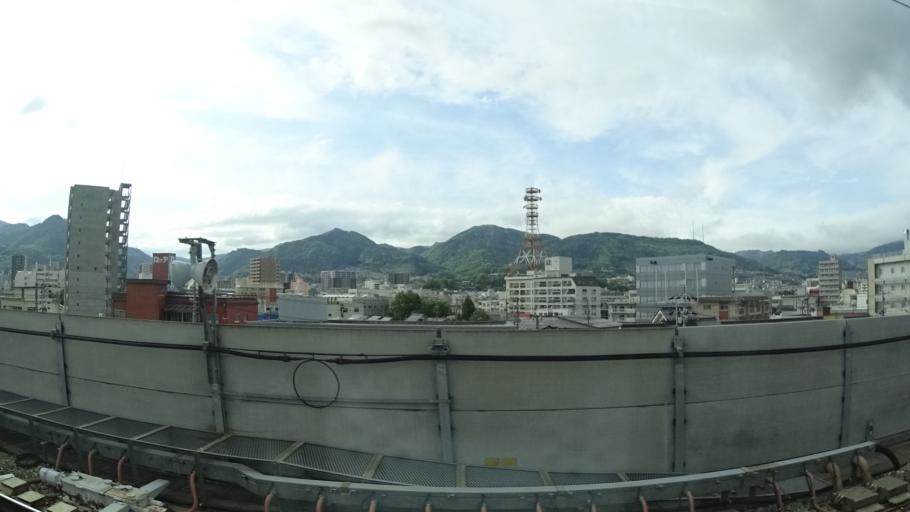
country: JP
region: Nagano
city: Nagano-shi
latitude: 36.6512
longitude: 138.2004
